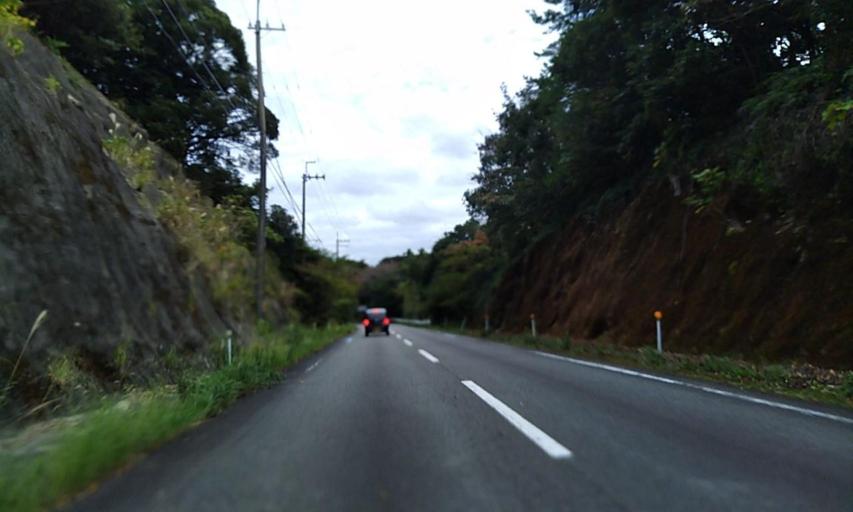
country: JP
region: Wakayama
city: Shingu
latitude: 33.4690
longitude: 135.8327
